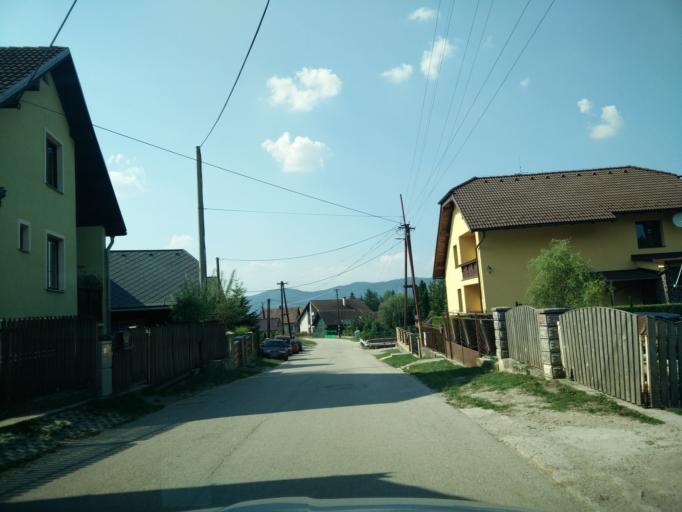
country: SK
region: Zilinsky
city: Rajec
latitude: 49.0956
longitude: 18.7142
